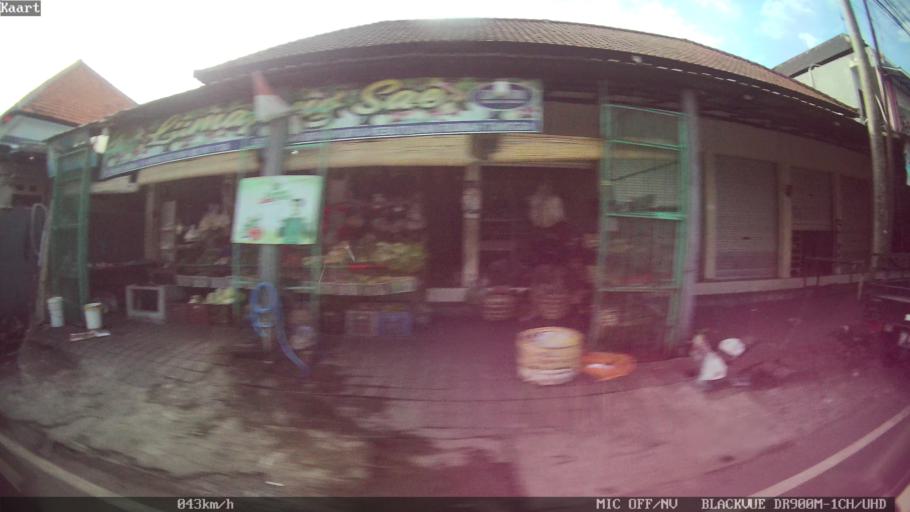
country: ID
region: Bali
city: Jabajero
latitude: -8.7182
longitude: 115.1878
